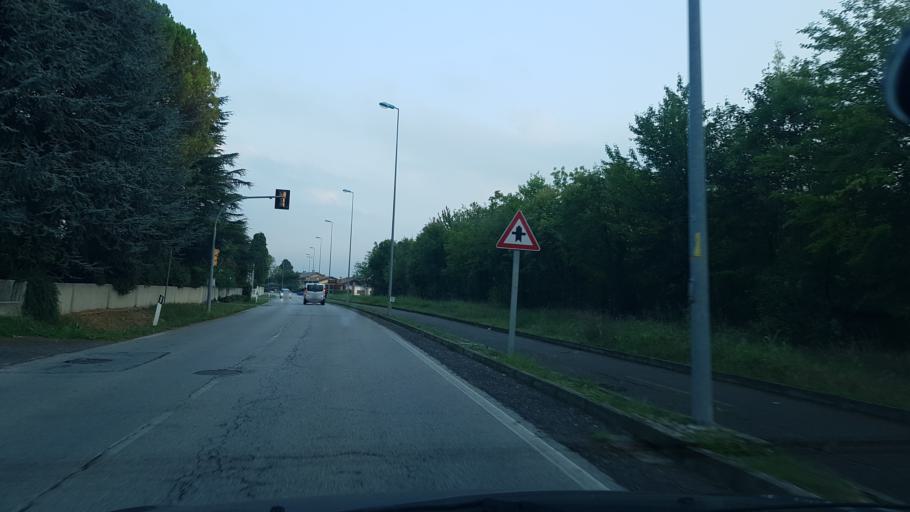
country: IT
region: Friuli Venezia Giulia
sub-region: Provincia di Udine
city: Trivignano Udinese
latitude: 45.9511
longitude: 13.3406
